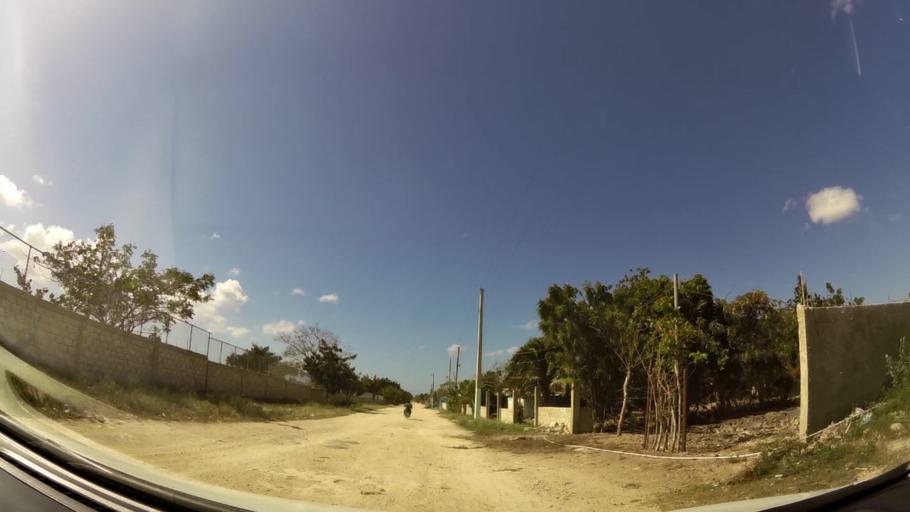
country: DO
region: Santo Domingo
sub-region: Santo Domingo
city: Boca Chica
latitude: 18.4630
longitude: -69.6229
